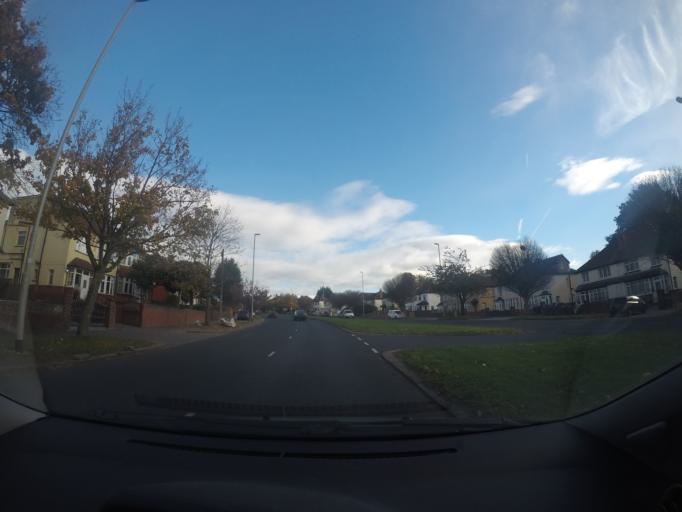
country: GB
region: England
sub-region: City and Borough of Leeds
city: Chapel Allerton
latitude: 53.8177
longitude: -1.5127
